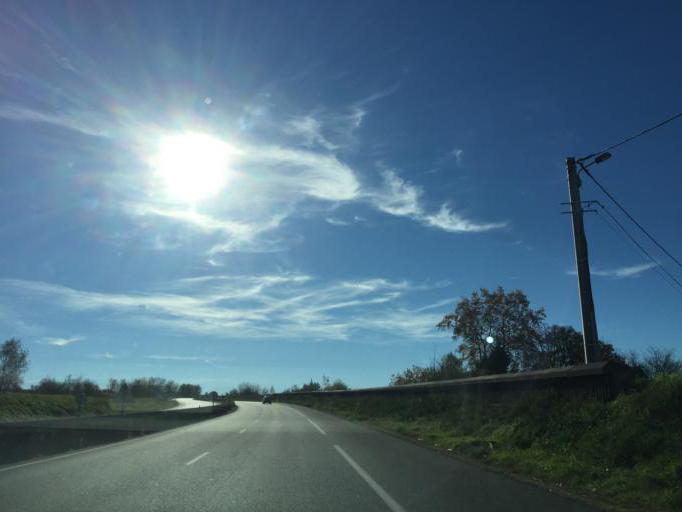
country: FR
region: Rhone-Alpes
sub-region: Departement de la Loire
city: Riorges
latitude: 46.0299
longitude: 4.0449
